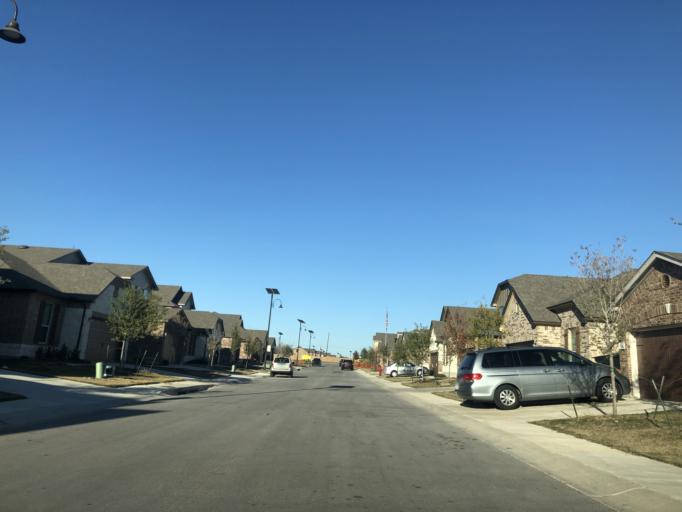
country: US
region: Texas
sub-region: Travis County
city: Windemere
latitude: 30.4724
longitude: -97.6589
